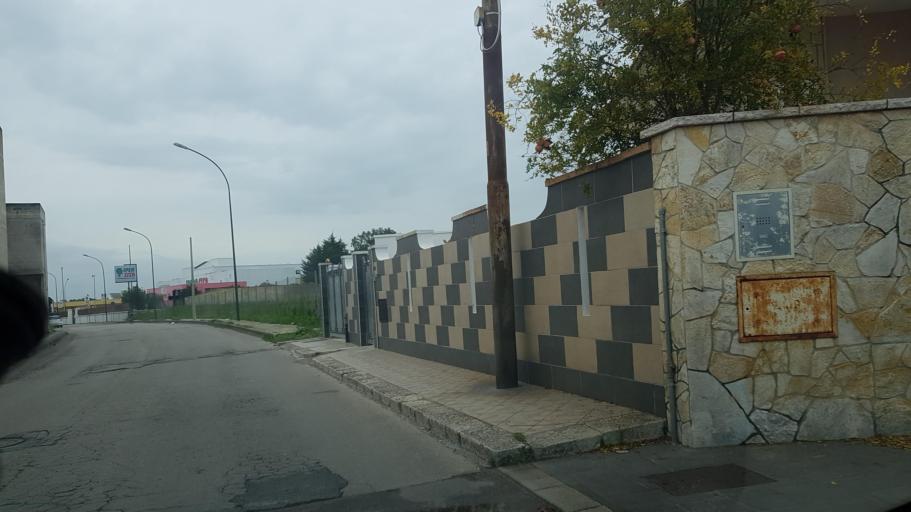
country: IT
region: Apulia
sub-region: Provincia di Lecce
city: Squinzano
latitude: 40.4367
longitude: 18.0323
